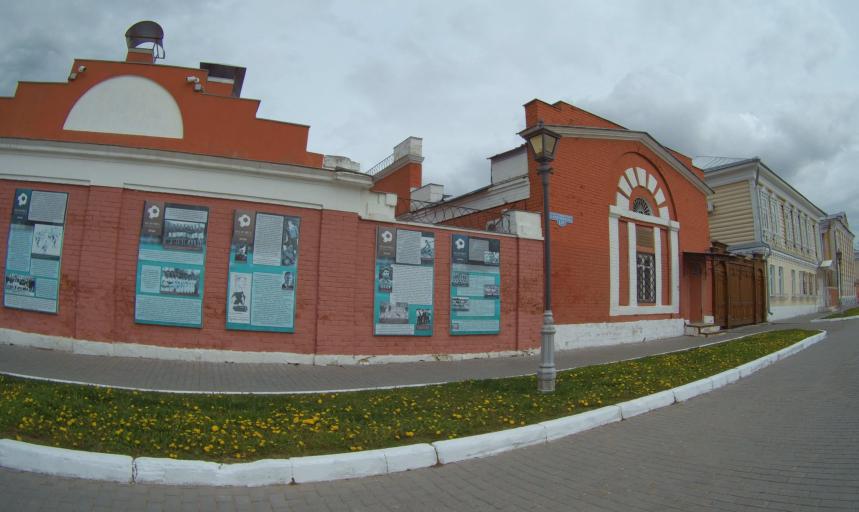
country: RU
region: Moskovskaya
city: Kolomna
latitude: 55.1048
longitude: 38.7539
